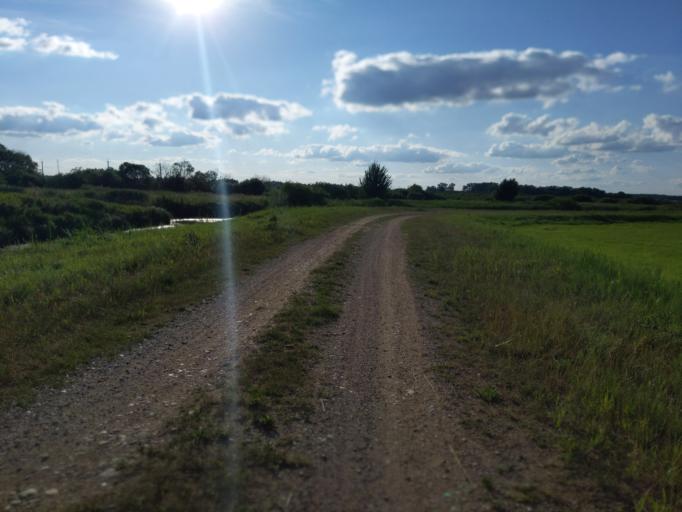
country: BY
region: Minsk
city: Nyasvizh
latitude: 53.2361
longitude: 26.7102
